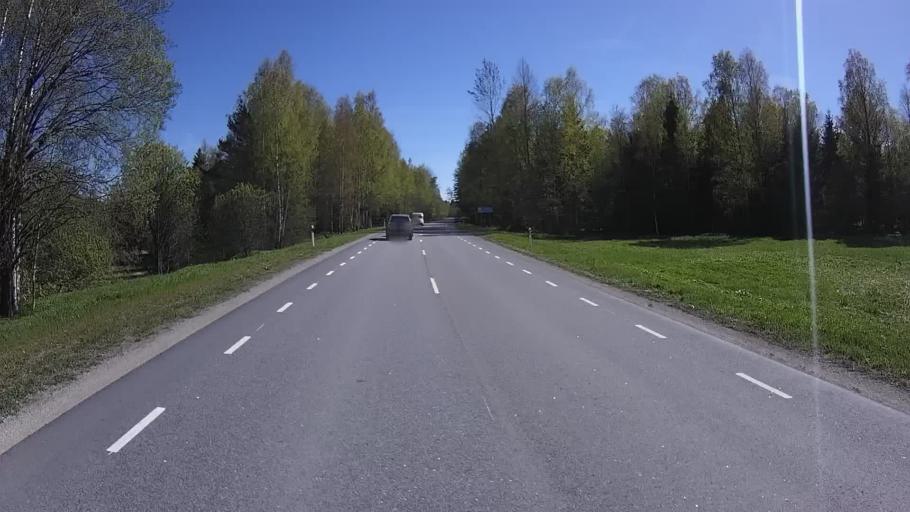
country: EE
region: Harju
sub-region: Loksa linn
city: Loksa
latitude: 59.5657
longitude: 25.7260
